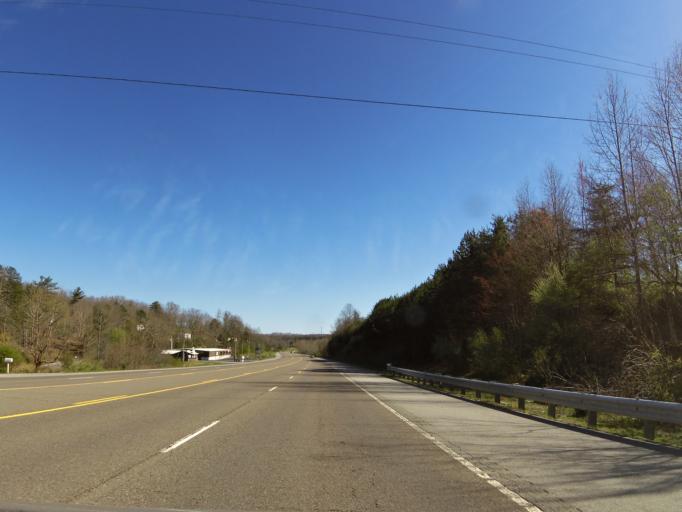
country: US
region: Tennessee
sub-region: Scott County
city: Oneida
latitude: 36.4547
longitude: -84.5457
